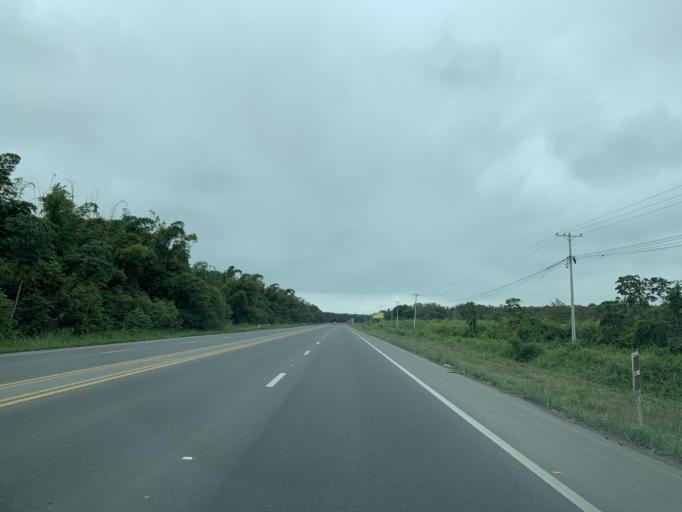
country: EC
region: Guayas
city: Coronel Marcelino Mariduena
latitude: -2.3244
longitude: -79.4528
